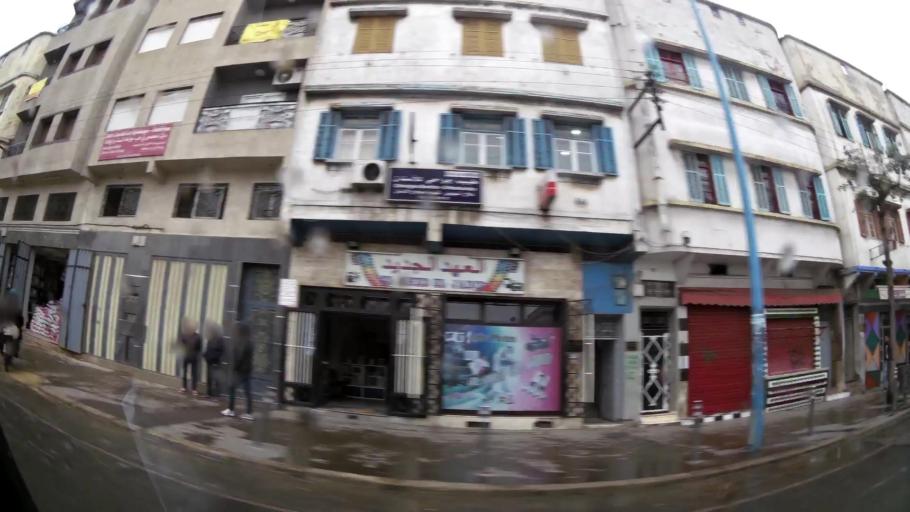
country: MA
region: Grand Casablanca
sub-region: Casablanca
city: Casablanca
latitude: 33.5522
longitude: -7.5792
